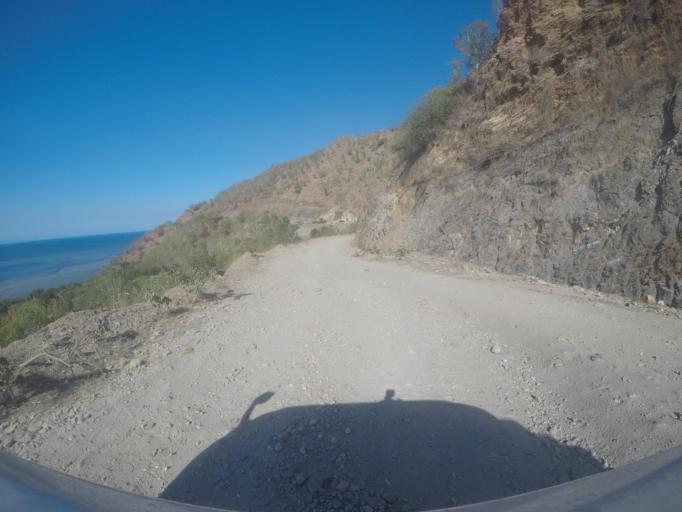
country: TL
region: Dili
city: Dili
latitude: -8.5290
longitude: 125.6239
